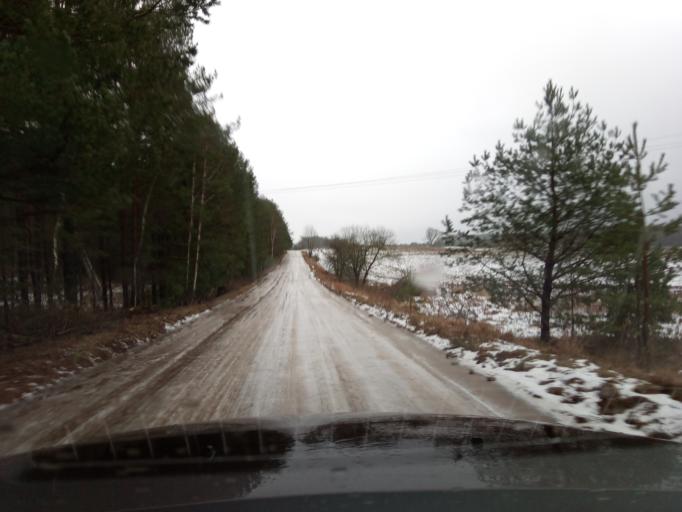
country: LT
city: Svencioneliai
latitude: 55.3456
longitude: 25.8343
